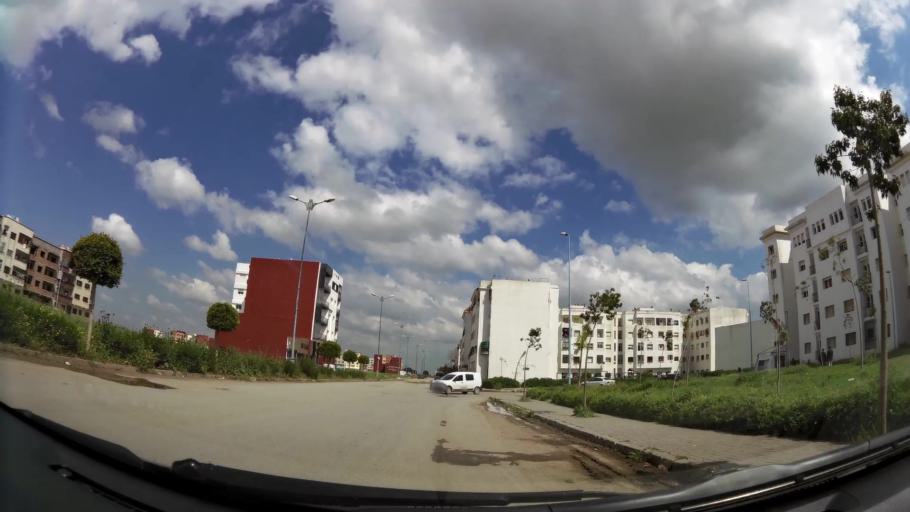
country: MA
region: Chaouia-Ouardigha
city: Nouaseur
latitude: 33.3616
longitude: -7.5428
